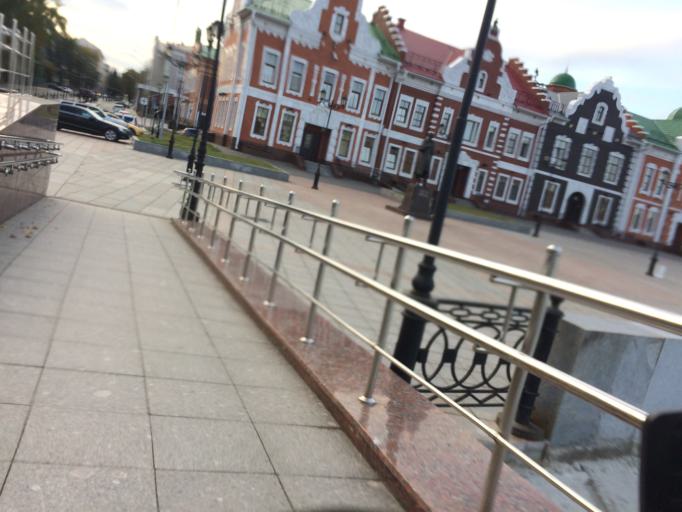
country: RU
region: Mariy-El
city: Yoshkar-Ola
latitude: 56.6296
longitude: 47.8994
